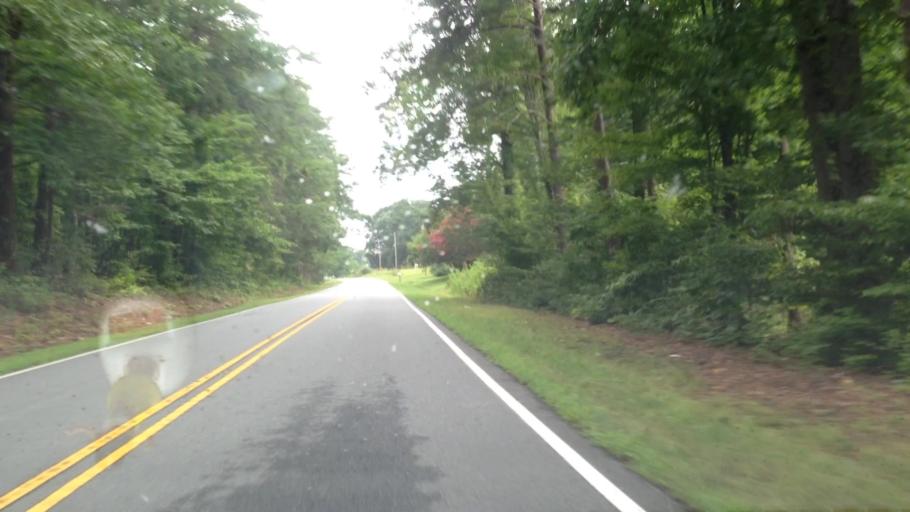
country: US
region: North Carolina
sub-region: Rockingham County
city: Mayodan
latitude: 36.4087
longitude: -80.0526
